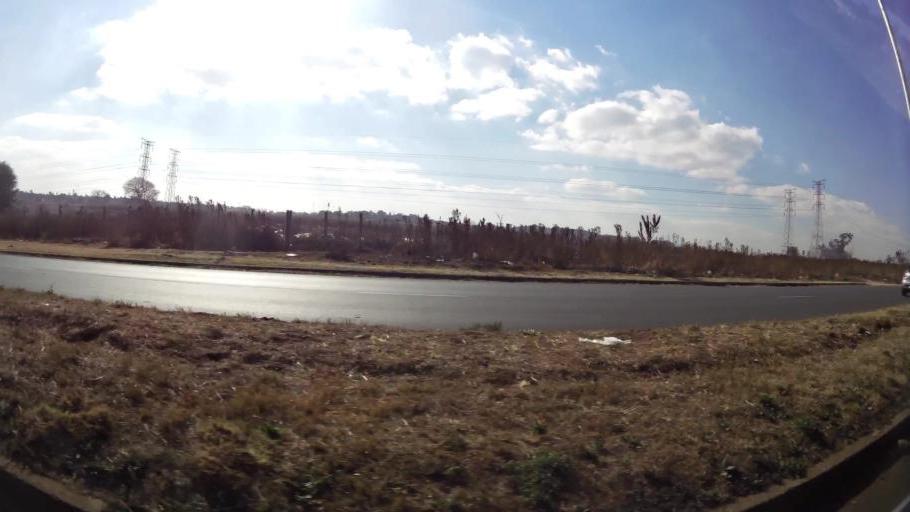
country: ZA
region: Gauteng
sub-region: City of Johannesburg Metropolitan Municipality
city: Soweto
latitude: -26.2829
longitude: 27.9156
